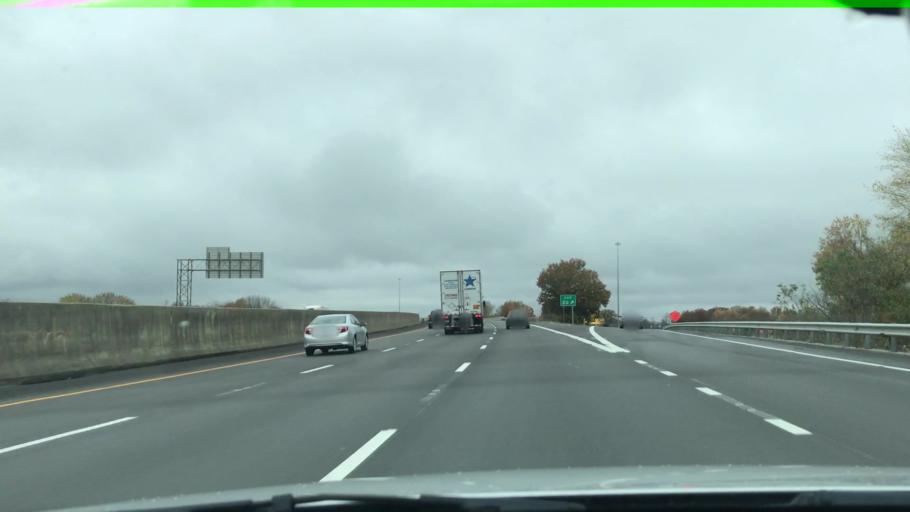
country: US
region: Kentucky
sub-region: Warren County
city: Bowling Green
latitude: 37.0070
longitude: -86.3665
